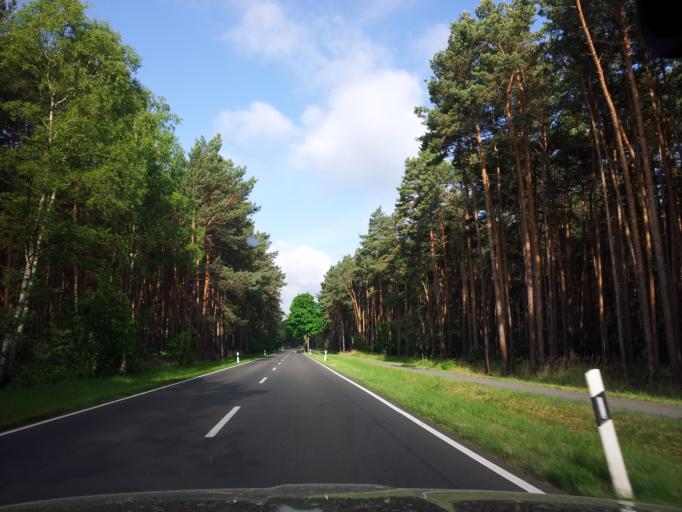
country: DE
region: Brandenburg
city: Linthe
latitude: 52.0950
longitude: 12.7843
